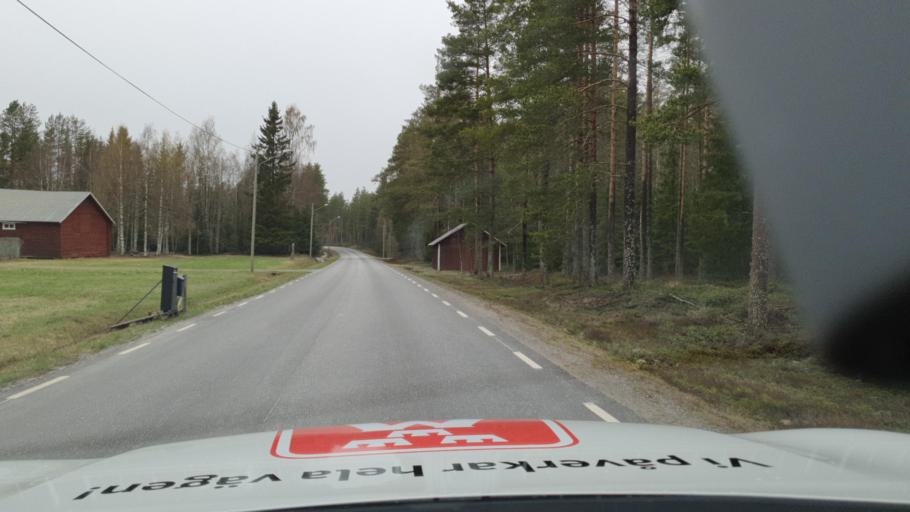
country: SE
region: Vaesterbotten
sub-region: Nordmalings Kommun
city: Nordmaling
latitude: 63.7055
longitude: 19.6060
